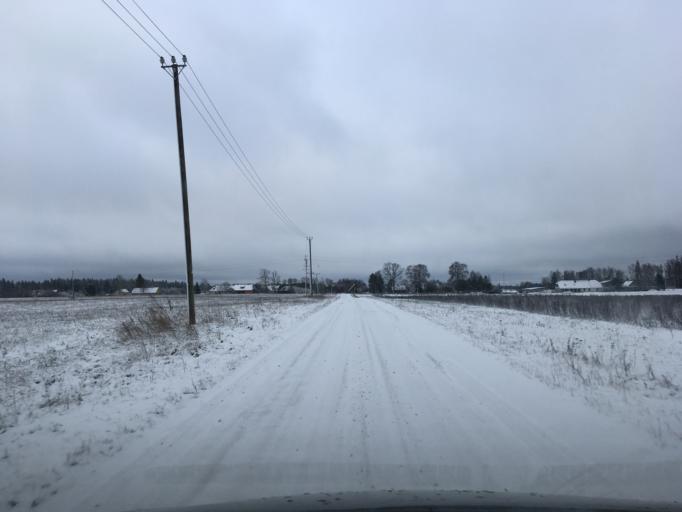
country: EE
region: Harju
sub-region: Raasiku vald
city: Raasiku
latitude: 59.2146
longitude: 25.1954
